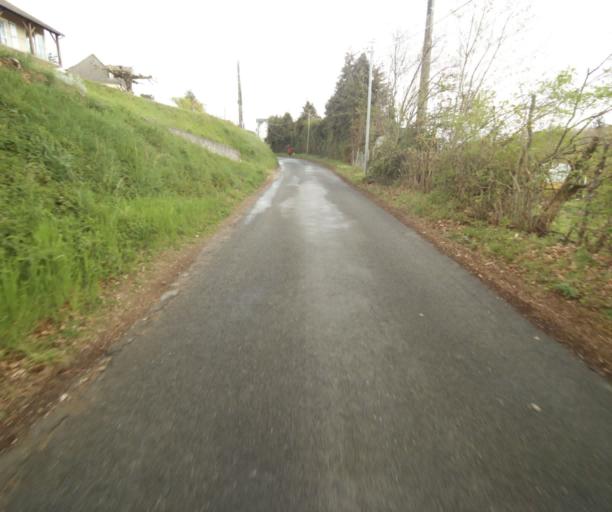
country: FR
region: Limousin
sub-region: Departement de la Correze
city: Tulle
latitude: 45.2746
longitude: 1.7509
